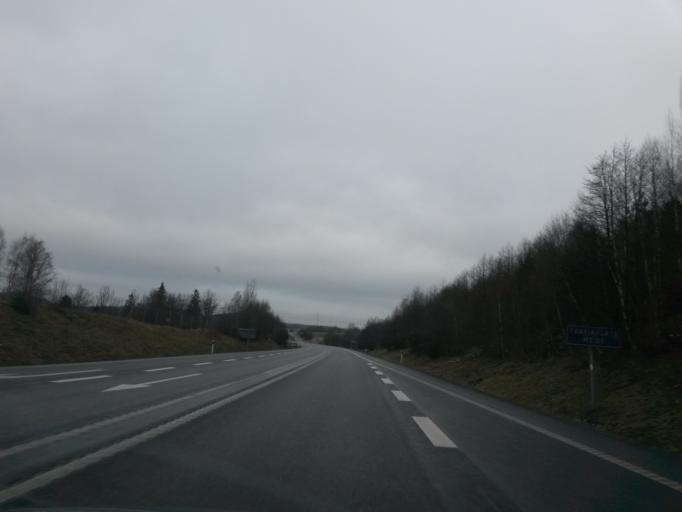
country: SE
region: Vaestra Goetaland
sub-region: Marks Kommun
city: Kinna
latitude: 57.4914
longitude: 12.6871
